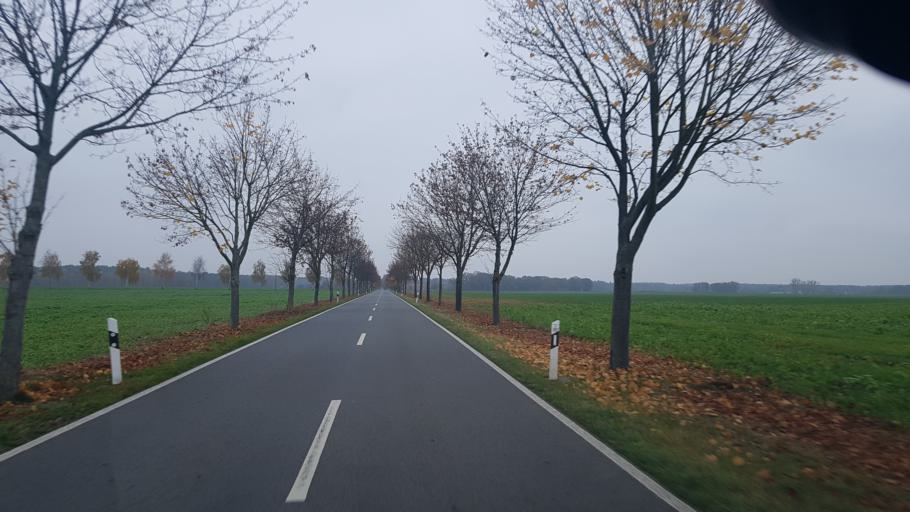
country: DE
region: Brandenburg
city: Lindow
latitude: 52.9431
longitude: 13.0140
